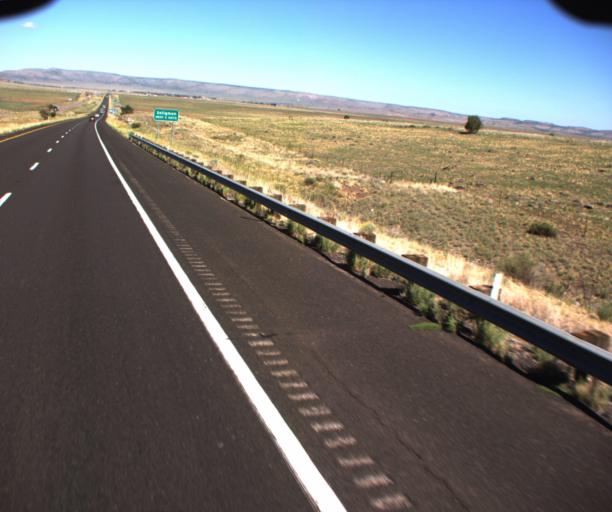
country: US
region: Arizona
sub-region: Yavapai County
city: Paulden
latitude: 35.2947
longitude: -112.8280
